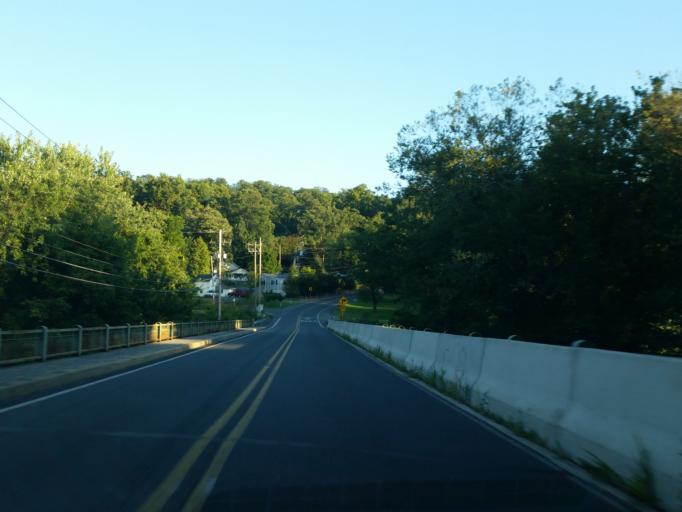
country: US
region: Pennsylvania
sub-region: Lebanon County
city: Jonestown
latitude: 40.4080
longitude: -76.4755
